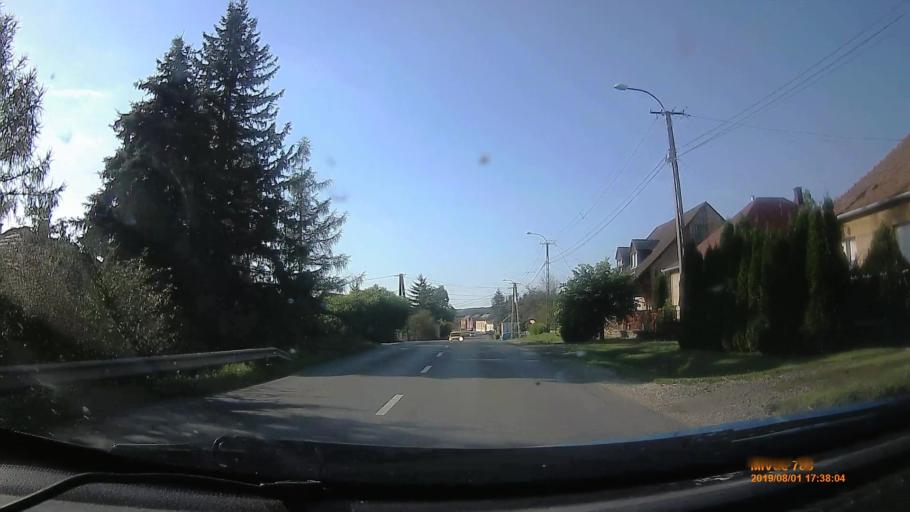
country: HU
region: Baranya
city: Komlo
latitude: 46.1922
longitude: 18.2006
